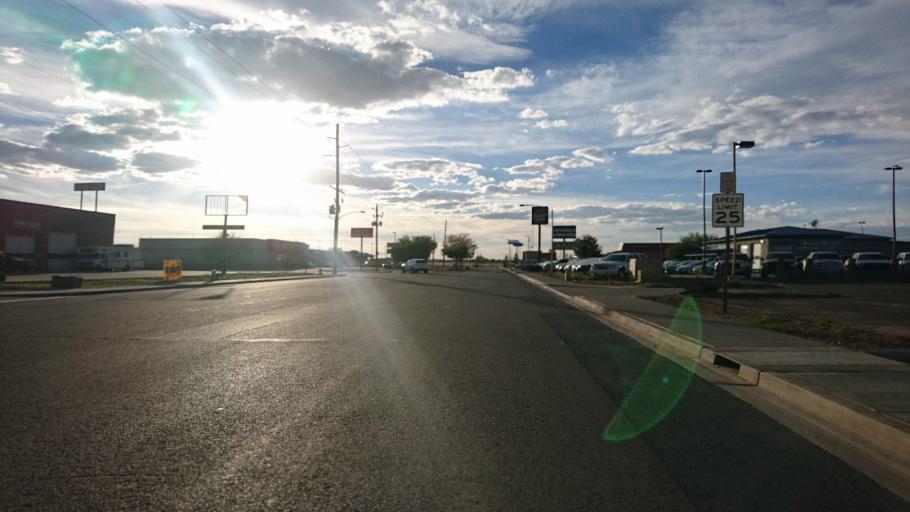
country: US
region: Arizona
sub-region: Navajo County
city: Winslow
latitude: 35.0409
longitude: -110.6989
